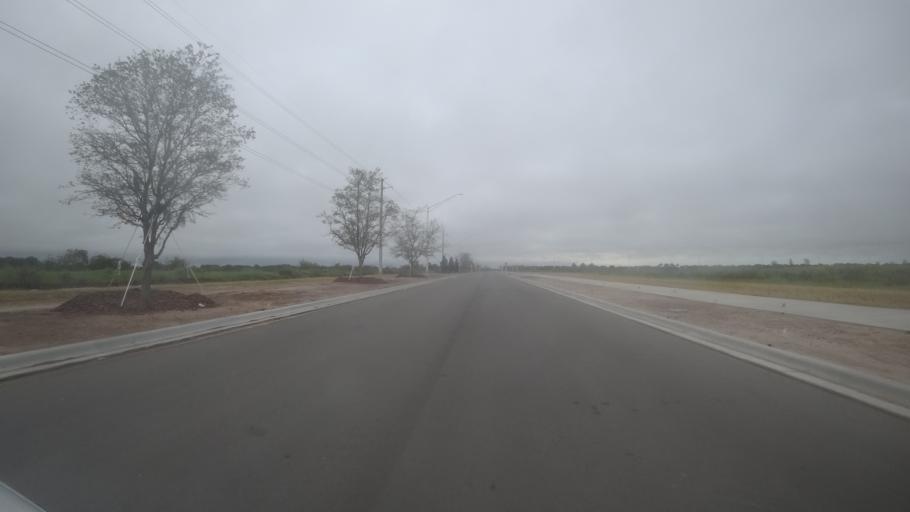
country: US
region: Florida
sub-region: Sarasota County
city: The Meadows
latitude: 27.4516
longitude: -82.3510
